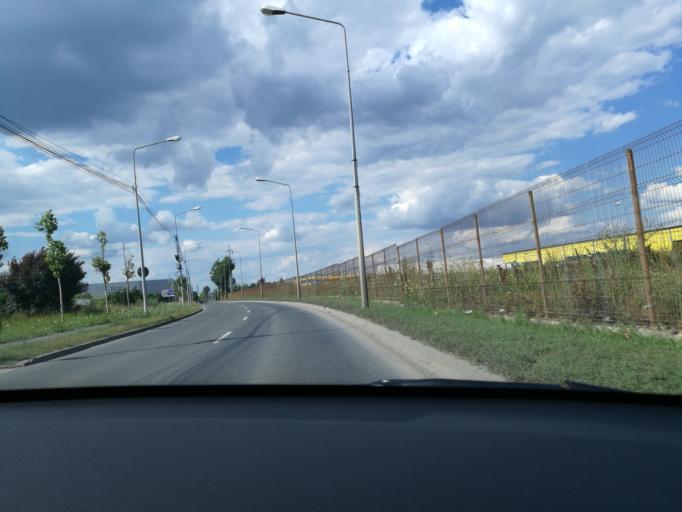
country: RO
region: Ilfov
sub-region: Comuna Glina
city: Catelu
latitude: 44.4084
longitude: 26.2185
